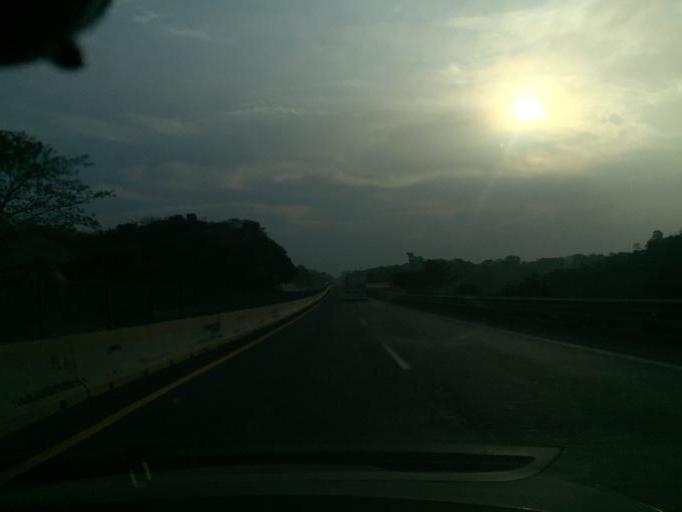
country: MX
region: Veracruz
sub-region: Omealca
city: Mata Tenatito (Casco Hacienda)
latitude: 18.7966
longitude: -96.5890
